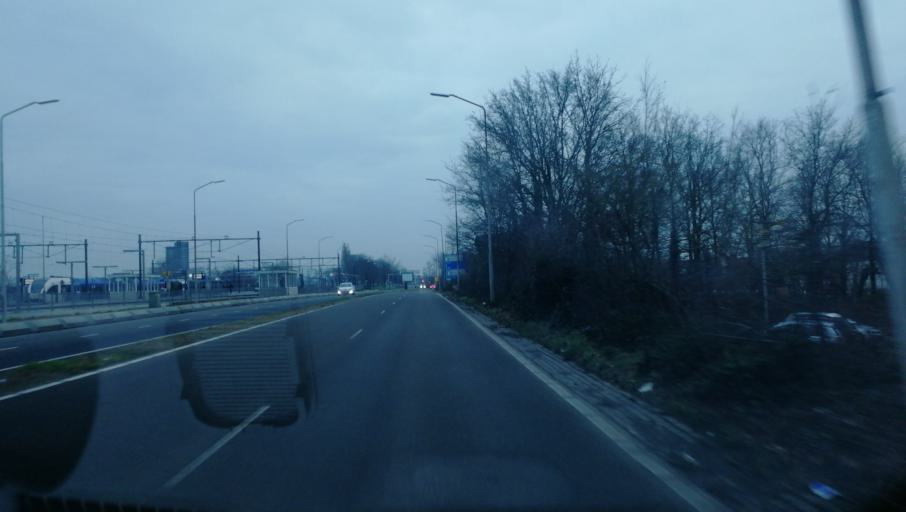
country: NL
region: Limburg
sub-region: Gemeente Venlo
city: Venlo
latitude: 51.3729
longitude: 6.1537
